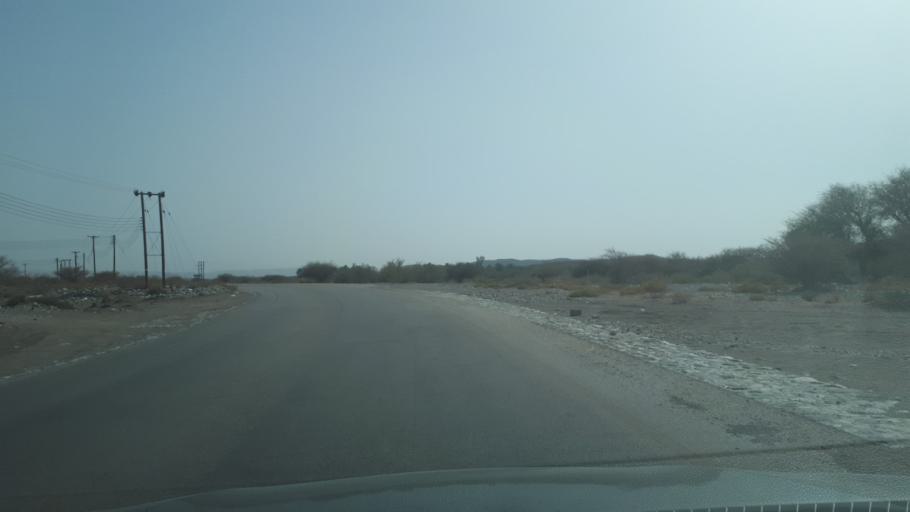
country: OM
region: Az Zahirah
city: `Ibri
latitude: 23.1451
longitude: 56.8968
